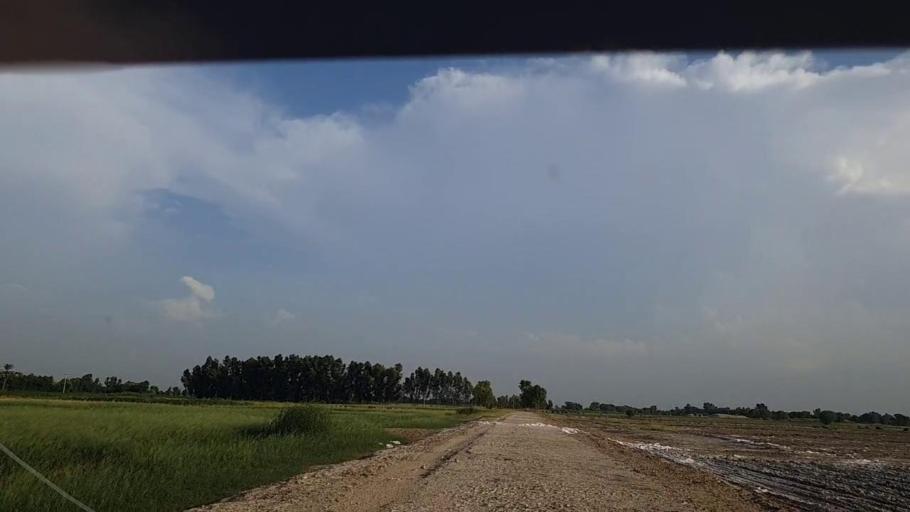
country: PK
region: Sindh
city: Khanpur
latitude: 27.8151
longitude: 69.3358
